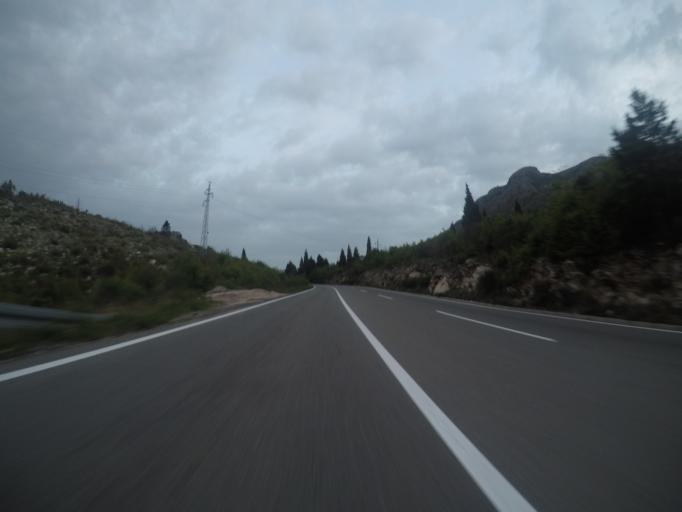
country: ME
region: Bar
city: Sutomore
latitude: 42.1732
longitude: 19.0006
